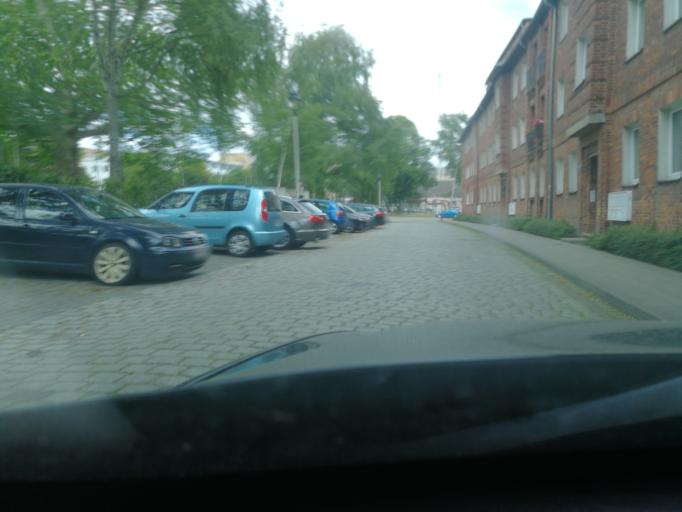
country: DE
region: Mecklenburg-Vorpommern
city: Stralsund
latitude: 54.3077
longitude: 13.0946
